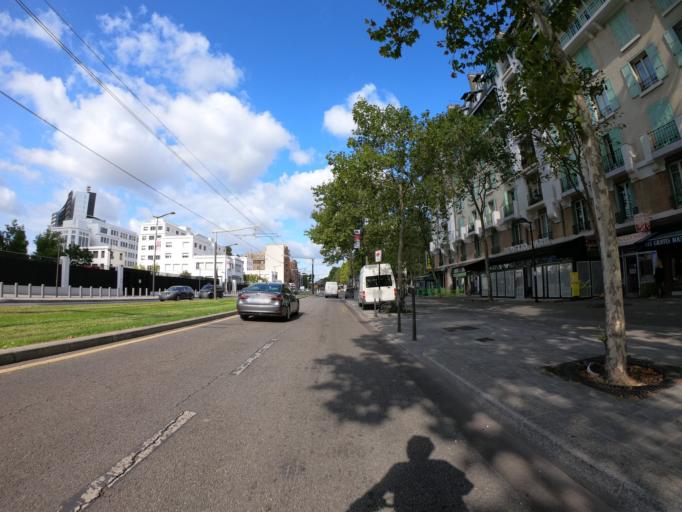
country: FR
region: Ile-de-France
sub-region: Departement des Hauts-de-Seine
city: Vanves
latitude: 48.8352
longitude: 2.2819
